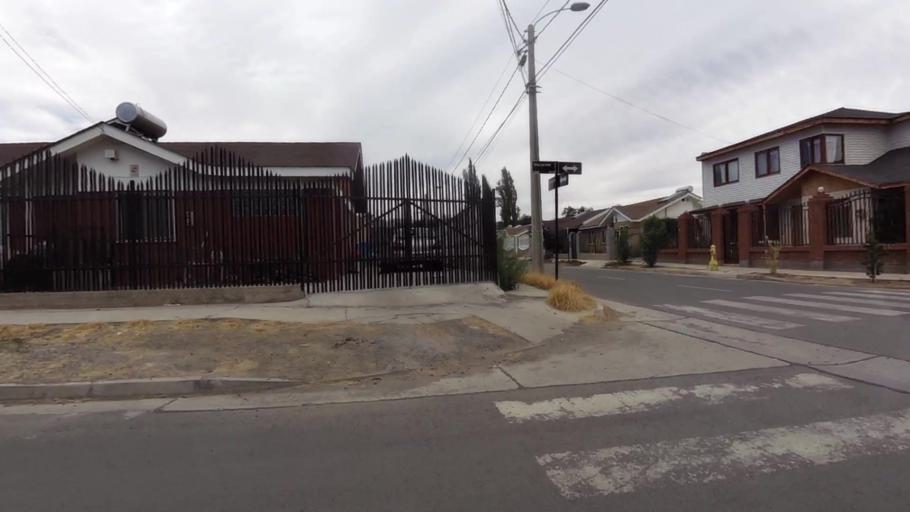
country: CL
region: O'Higgins
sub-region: Provincia de Cachapoal
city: Graneros
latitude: -34.0818
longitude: -70.7379
